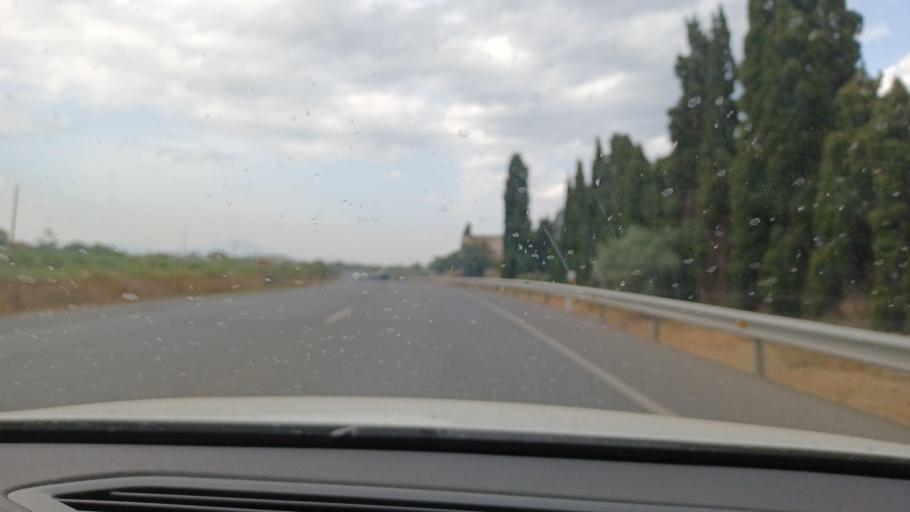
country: ES
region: Valencia
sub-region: Provincia de Castello
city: Benicarlo
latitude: 40.4446
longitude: 0.4467
